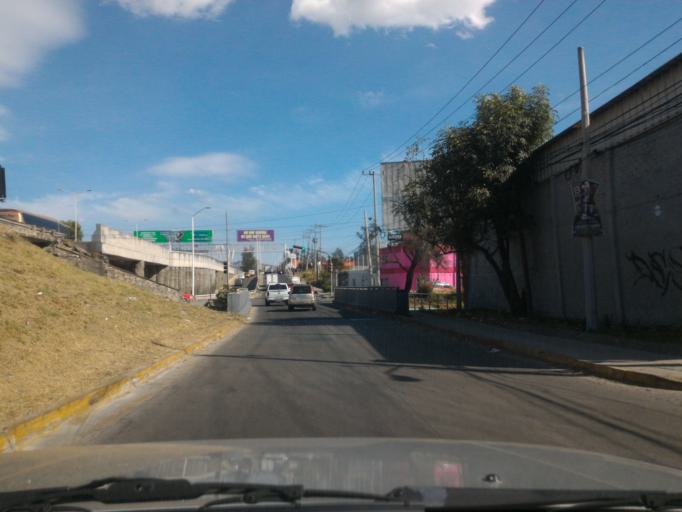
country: MX
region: Jalisco
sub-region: Tlajomulco de Zuniga
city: La Tijera
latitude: 20.6118
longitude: -103.4221
